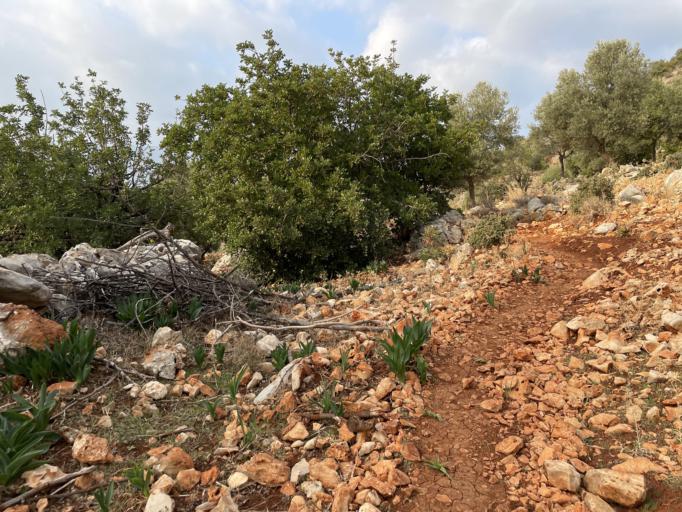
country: TR
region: Antalya
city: Kas
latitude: 36.1672
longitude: 29.6535
